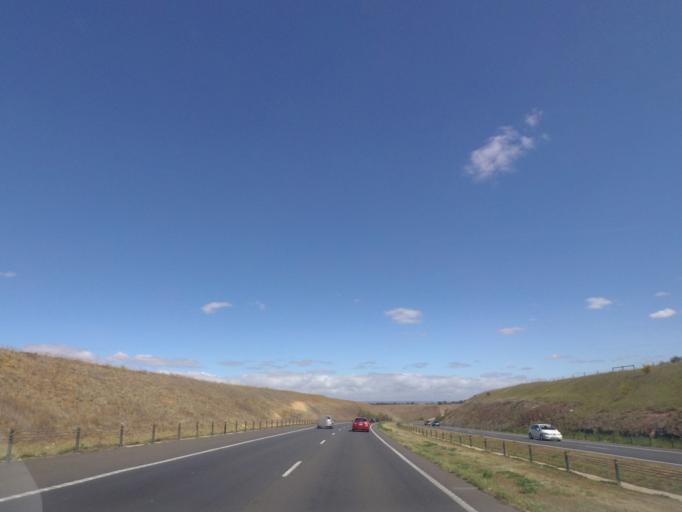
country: AU
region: Victoria
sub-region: Melton
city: Brookfield
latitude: -37.6886
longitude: 144.5240
